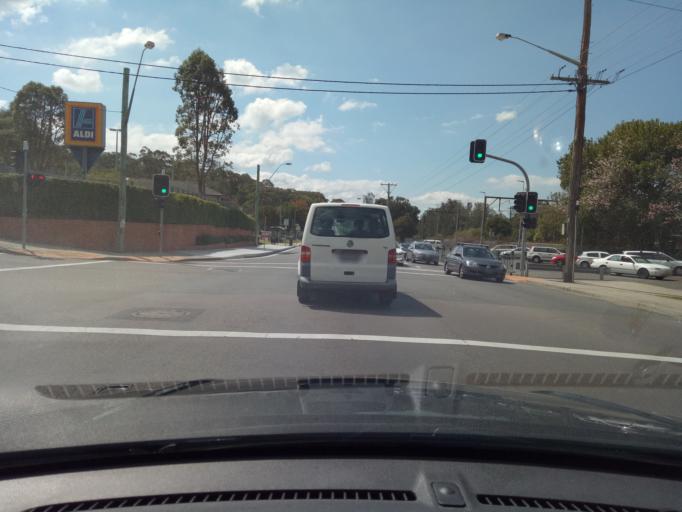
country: AU
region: New South Wales
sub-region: Gosford Shire
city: Point Clare
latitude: -33.4461
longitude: 151.3281
